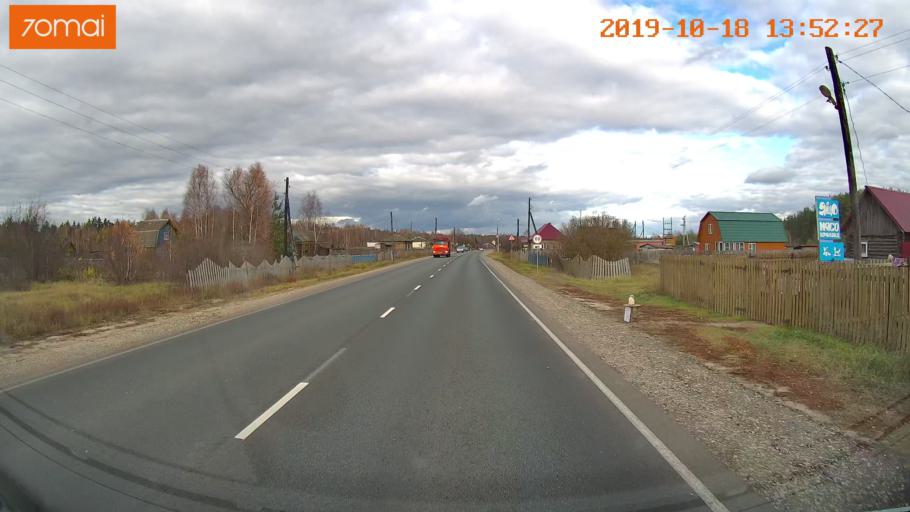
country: RU
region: Moskovskaya
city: Radovitskiy
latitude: 55.0302
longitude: 39.9684
